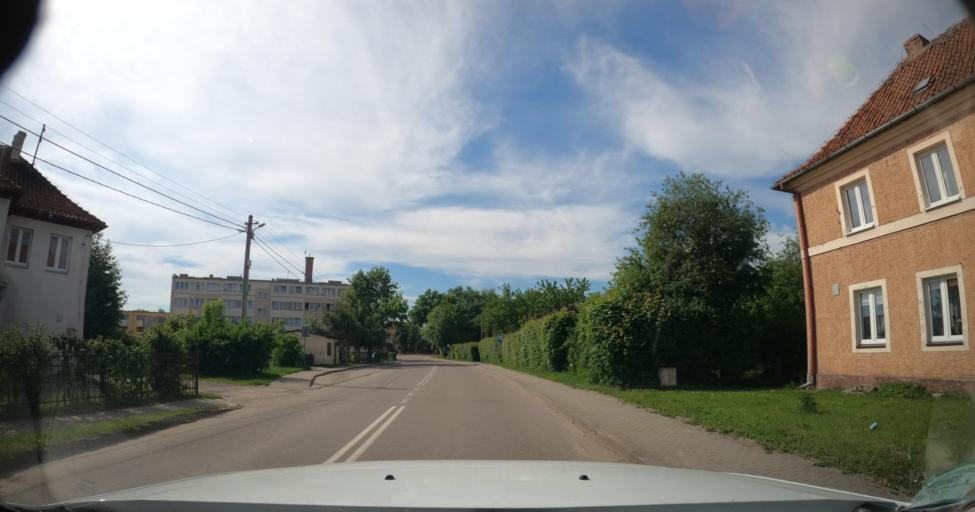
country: PL
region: Warmian-Masurian Voivodeship
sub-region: Powiat ostrodzki
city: Milakowo
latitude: 54.0088
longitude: 20.0778
